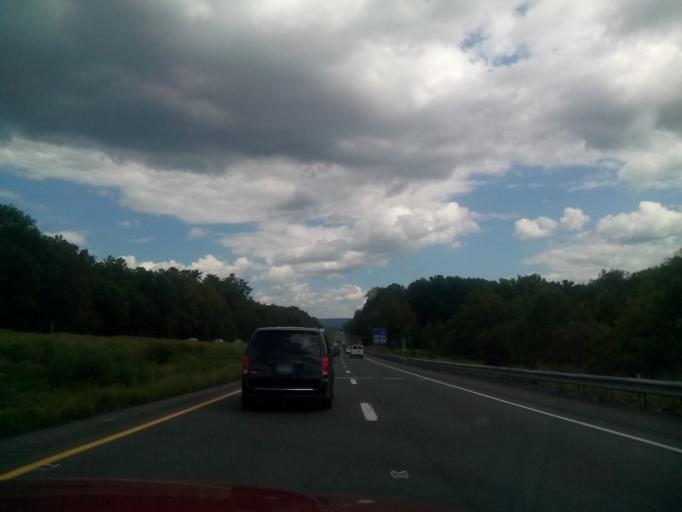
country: US
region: Pennsylvania
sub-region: Monroe County
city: Arlington Heights
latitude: 40.9951
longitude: -75.2618
